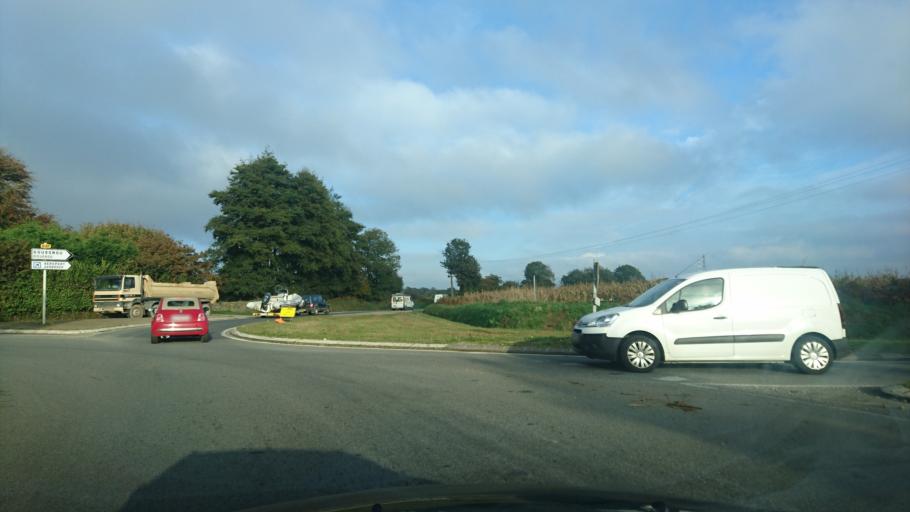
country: FR
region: Brittany
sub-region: Departement du Finistere
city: Bohars
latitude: 48.4488
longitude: -4.5115
